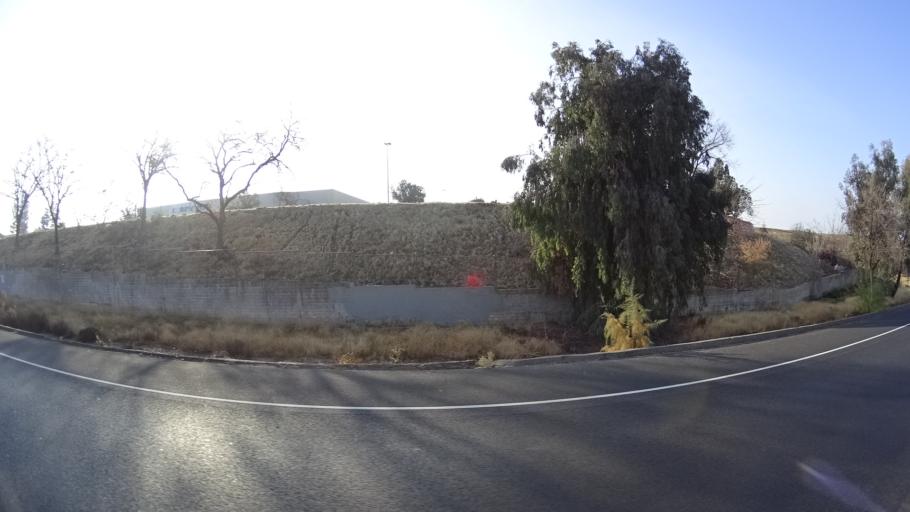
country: US
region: California
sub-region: Kern County
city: Bakersfield
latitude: 35.3957
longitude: -118.9628
